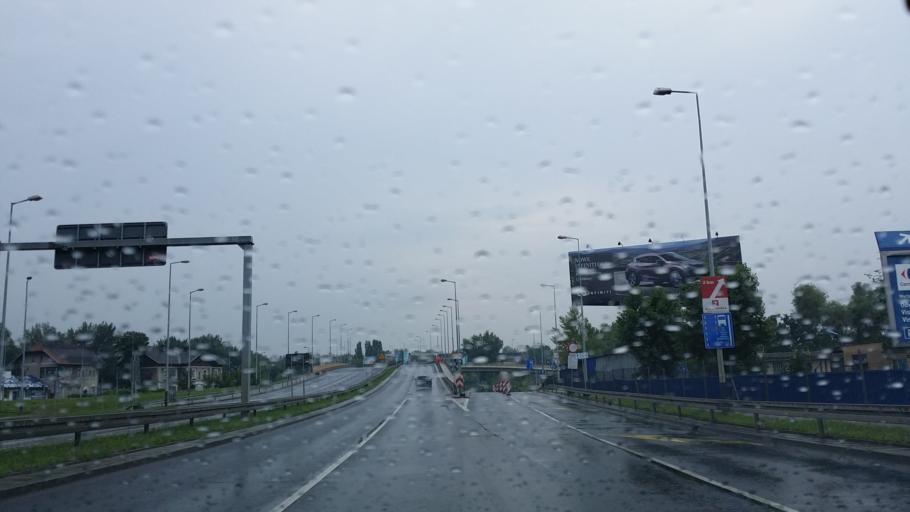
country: PL
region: Lesser Poland Voivodeship
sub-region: Krakow
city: Krakow
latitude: 50.0314
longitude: 19.9453
